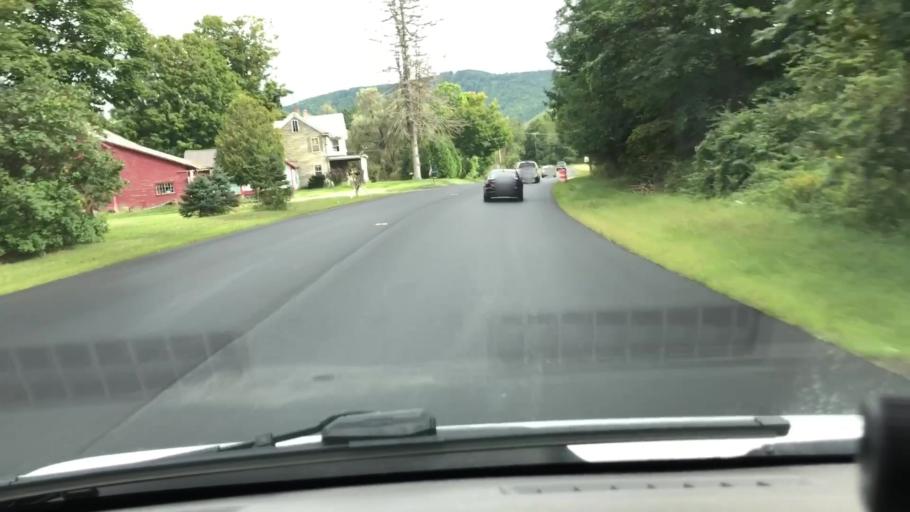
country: US
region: Massachusetts
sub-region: Franklin County
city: Charlemont
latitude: 42.6317
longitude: -72.8957
